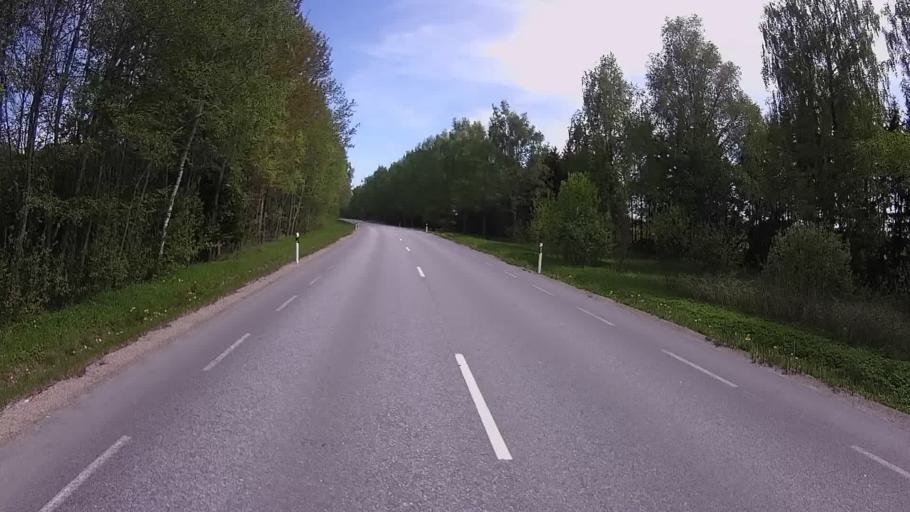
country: EE
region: Valgamaa
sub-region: Valga linn
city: Valga
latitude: 57.7319
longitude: 26.1551
